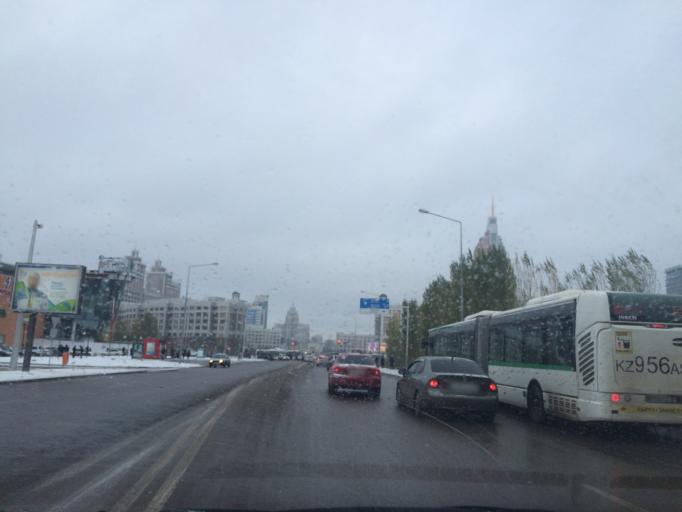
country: KZ
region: Astana Qalasy
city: Astana
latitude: 51.1267
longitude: 71.4129
